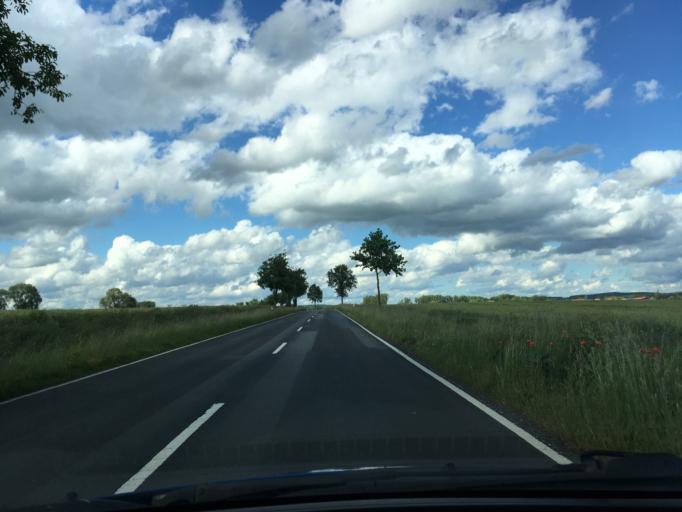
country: DE
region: Lower Saxony
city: Hardegsen
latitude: 51.6307
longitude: 9.8547
